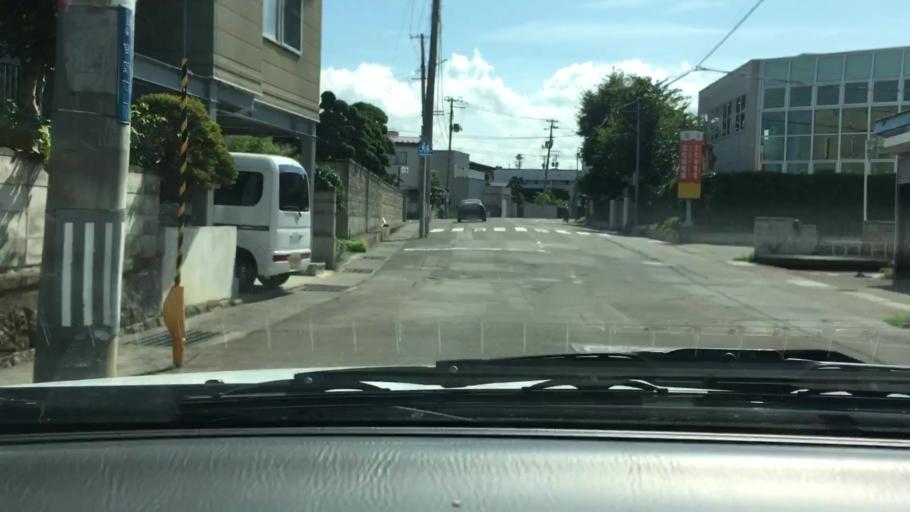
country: JP
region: Aomori
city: Hirosaki
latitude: 40.5961
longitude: 140.4704
